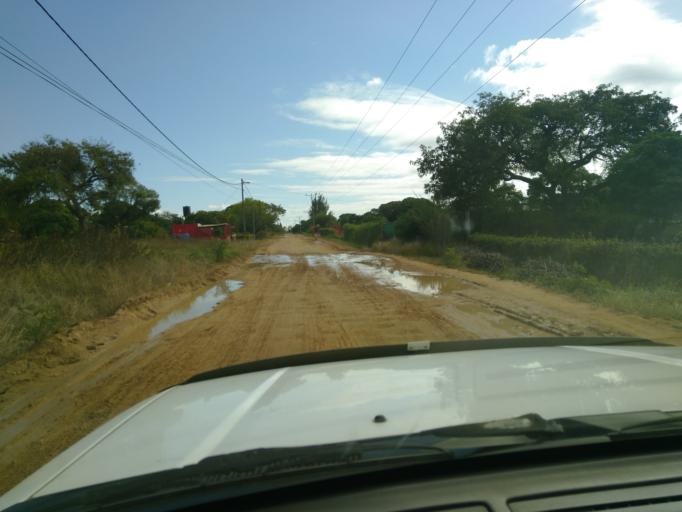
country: MZ
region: Maputo City
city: Maputo
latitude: -25.9993
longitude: 32.5414
